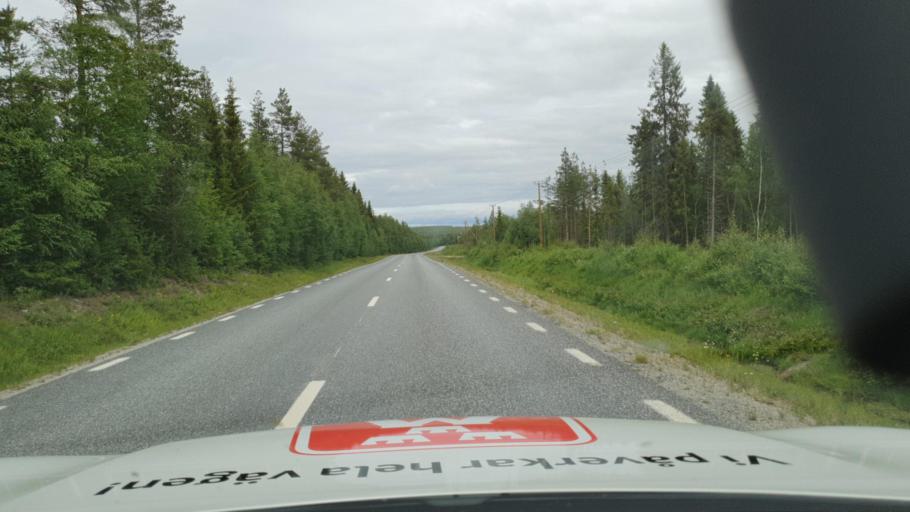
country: SE
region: Vaesterbotten
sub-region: Asele Kommun
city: Insjon
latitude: 64.2698
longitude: 17.5756
